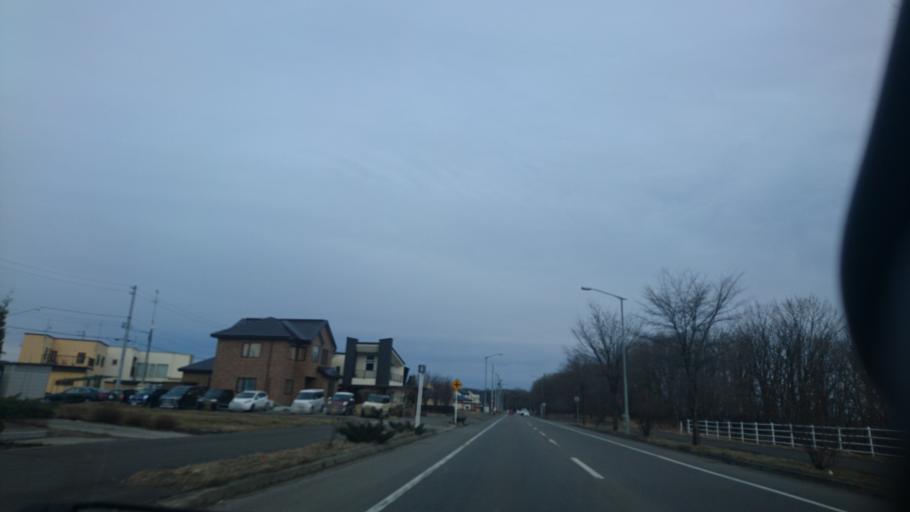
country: JP
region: Hokkaido
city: Obihiro
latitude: 42.9488
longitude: 143.1890
